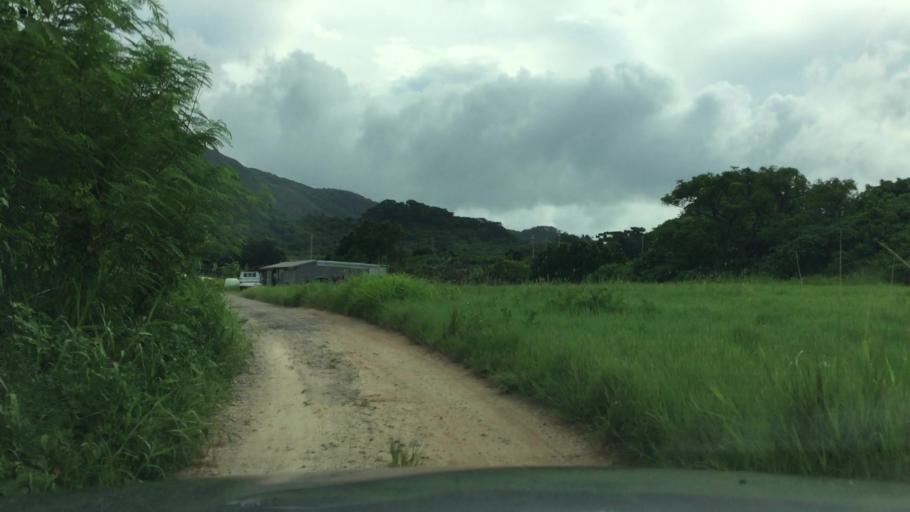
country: JP
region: Okinawa
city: Ishigaki
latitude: 24.4677
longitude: 124.1378
